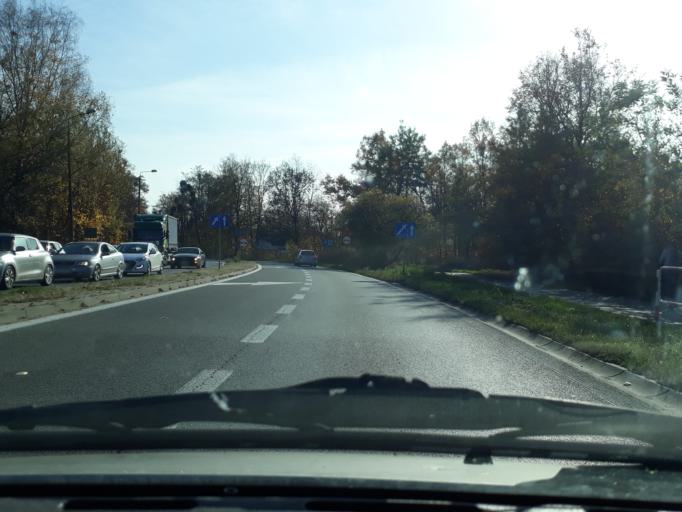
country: PL
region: Silesian Voivodeship
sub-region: Powiat tarnogorski
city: Tarnowskie Gory
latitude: 50.4420
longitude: 18.8356
